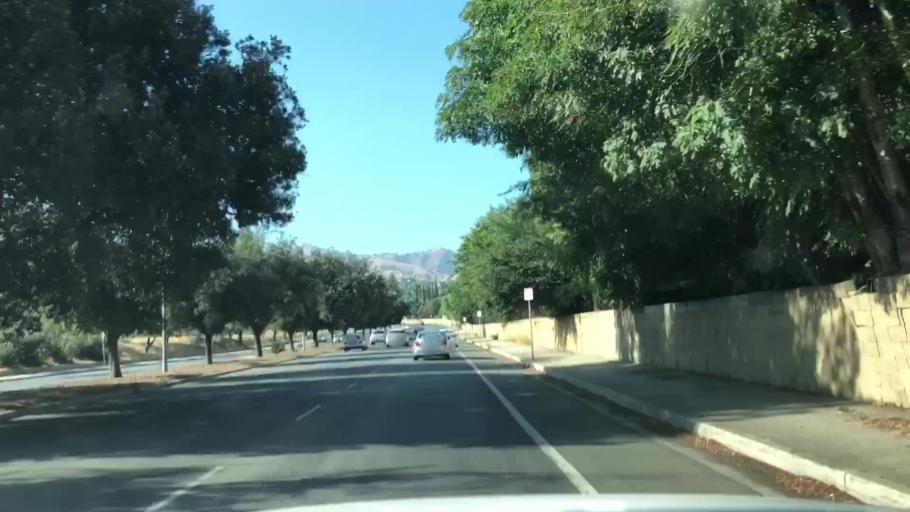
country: US
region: California
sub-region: Los Angeles County
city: Northridge
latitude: 34.2671
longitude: -118.5550
